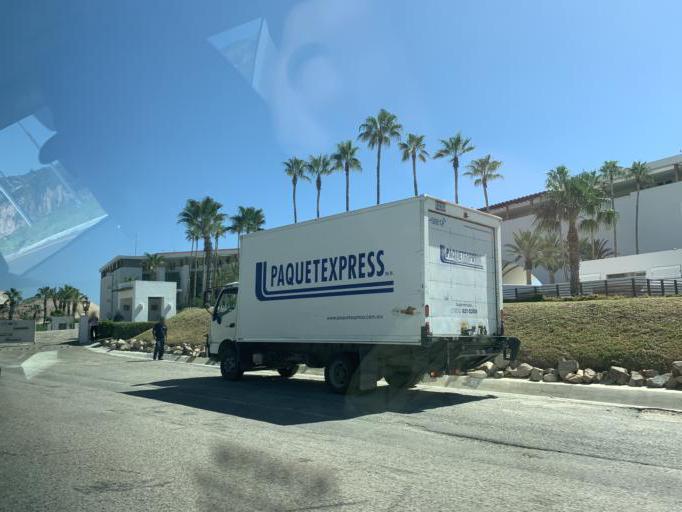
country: MX
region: Baja California Sur
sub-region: Los Cabos
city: San Jose del Cabo
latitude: 22.9865
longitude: -109.7586
